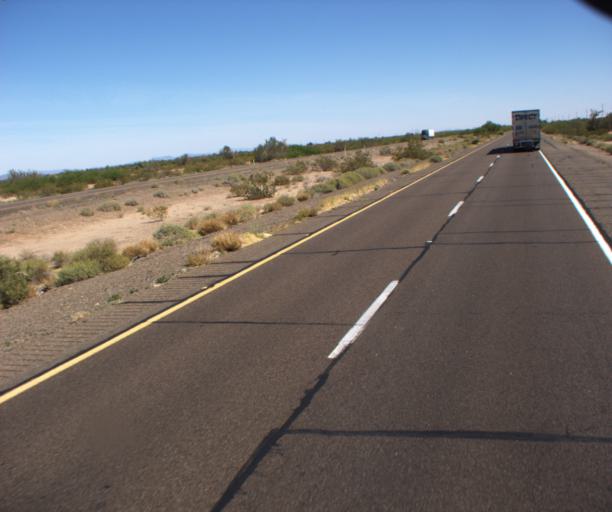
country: US
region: Arizona
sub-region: Yuma County
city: Wellton
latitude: 32.8208
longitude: -113.4709
